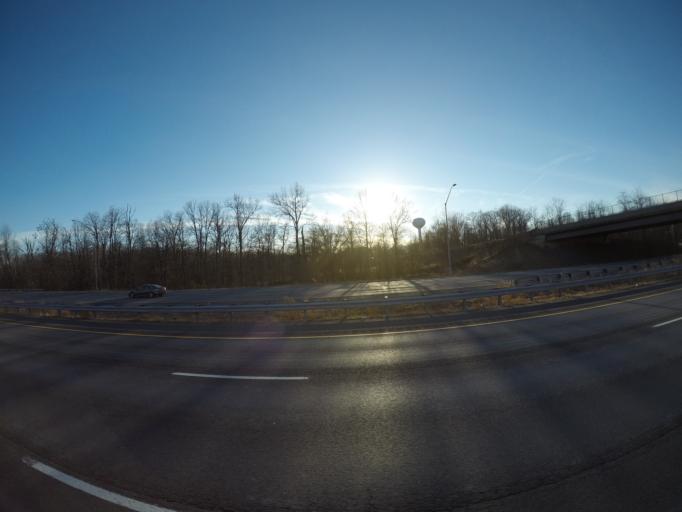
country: US
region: Maryland
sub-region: Howard County
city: Columbia
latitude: 39.2238
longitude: -76.8060
